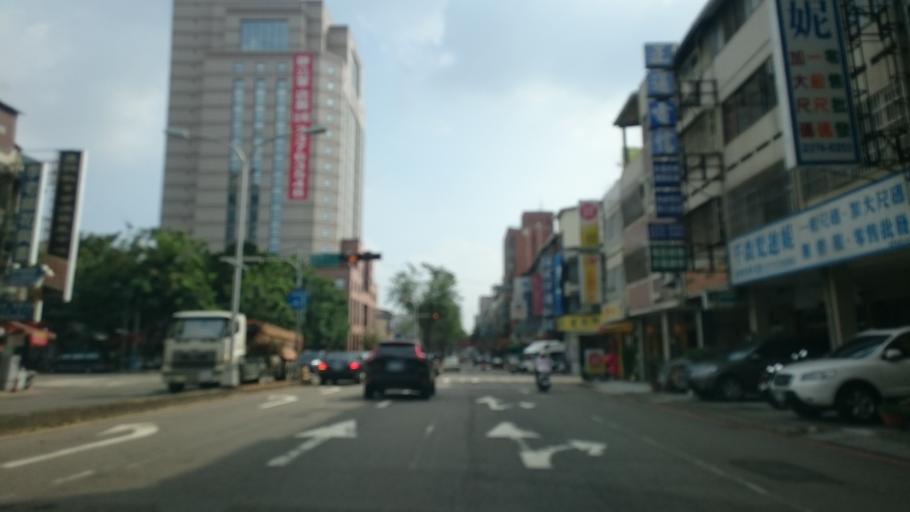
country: TW
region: Taiwan
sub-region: Taichung City
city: Taichung
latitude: 24.1371
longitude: 120.6572
